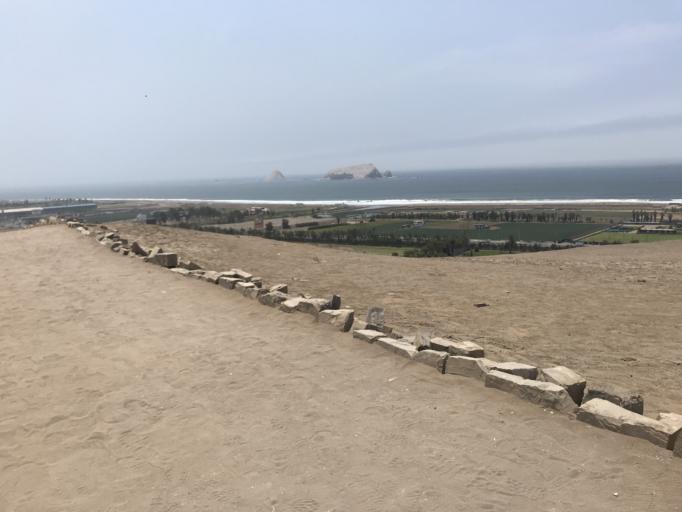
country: PE
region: Lima
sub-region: Lima
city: Punta Hermosa
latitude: -12.2628
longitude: -76.9027
